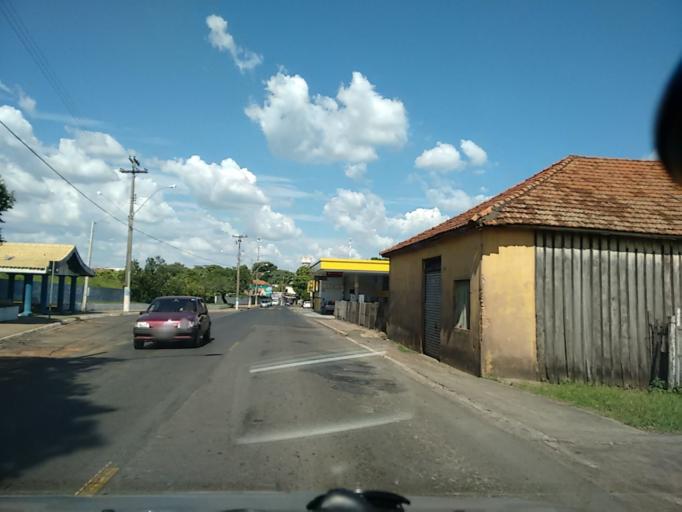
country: BR
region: Sao Paulo
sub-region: Pompeia
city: Pompeia
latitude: -22.1032
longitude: -50.1825
